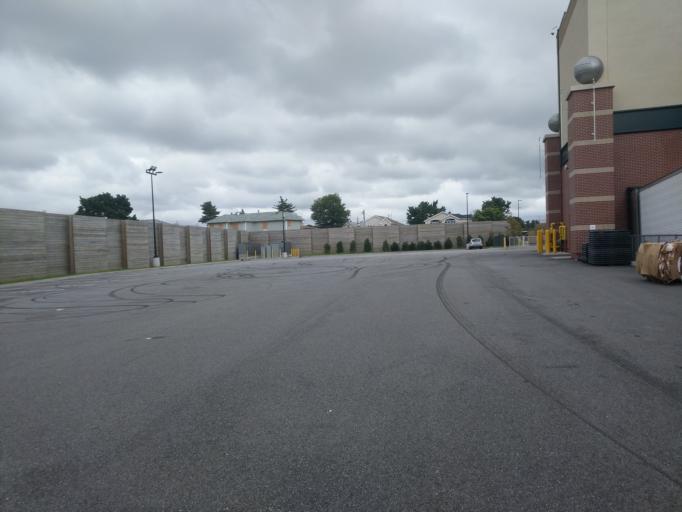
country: US
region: New York
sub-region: Nassau County
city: South Valley Stream
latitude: 40.6624
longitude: -73.7278
